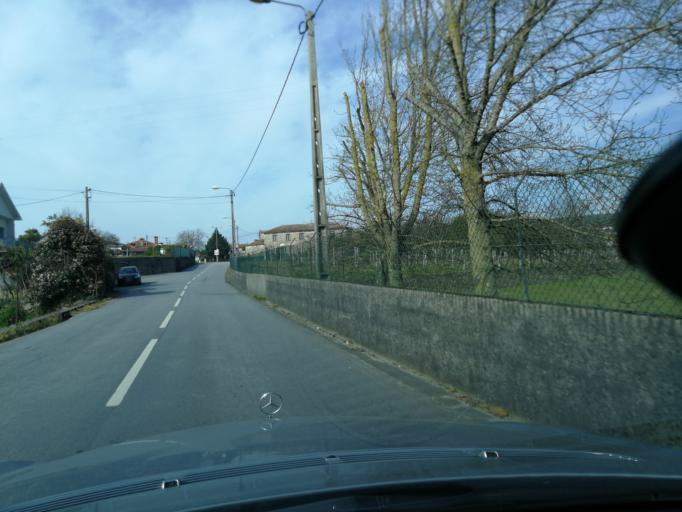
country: PT
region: Braga
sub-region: Vila Nova de Famalicao
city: Vila Nova de Famalicao
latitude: 41.4334
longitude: -8.5219
